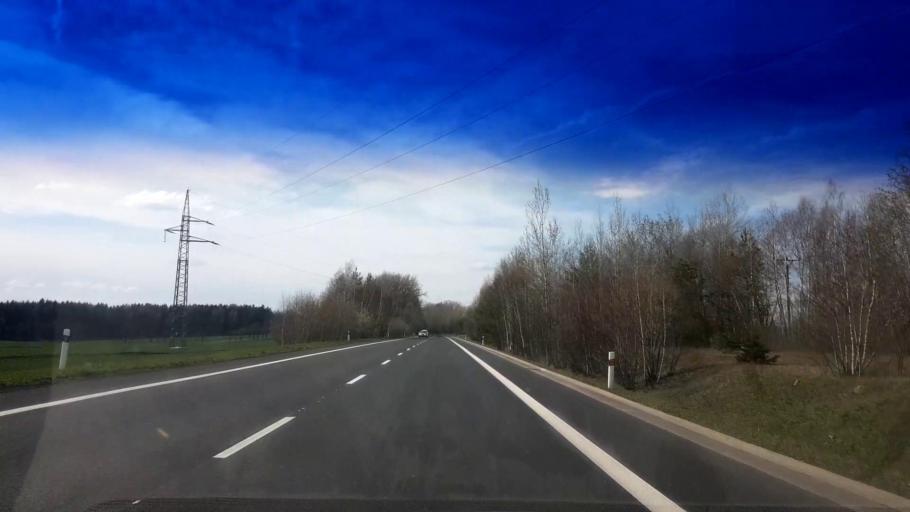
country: CZ
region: Karlovarsky
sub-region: Okres Cheb
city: Frantiskovy Lazne
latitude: 50.0962
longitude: 12.3368
